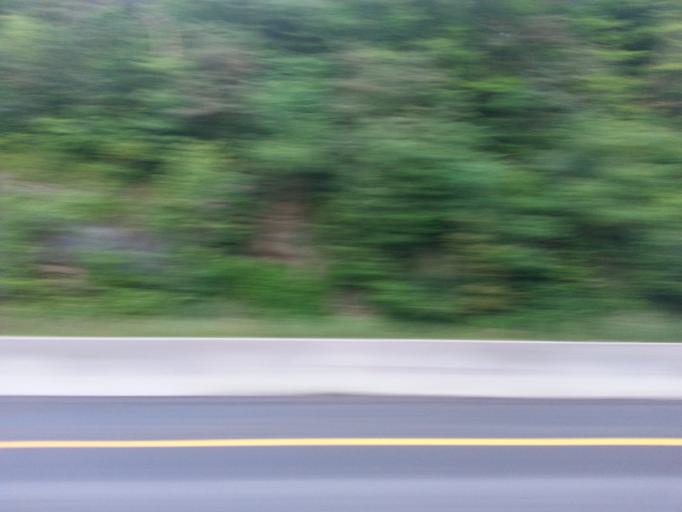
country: US
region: Tennessee
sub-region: Campbell County
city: Jellico
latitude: 36.5458
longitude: -84.1506
